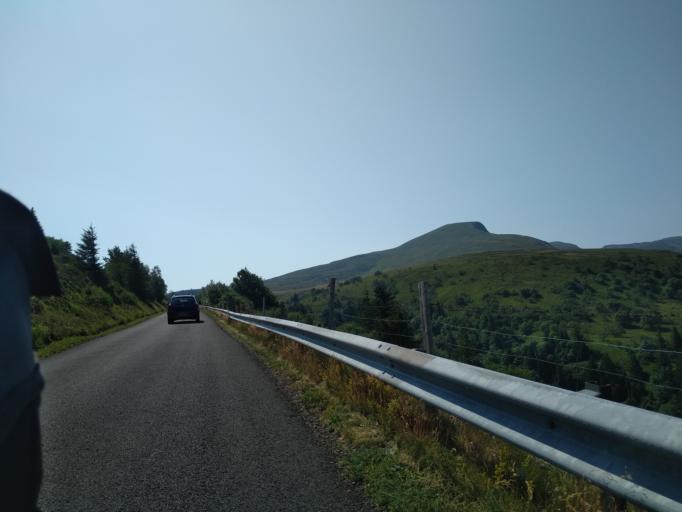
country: FR
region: Auvergne
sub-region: Departement du Puy-de-Dome
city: Mont-Dore
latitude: 45.5672
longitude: 2.8217
